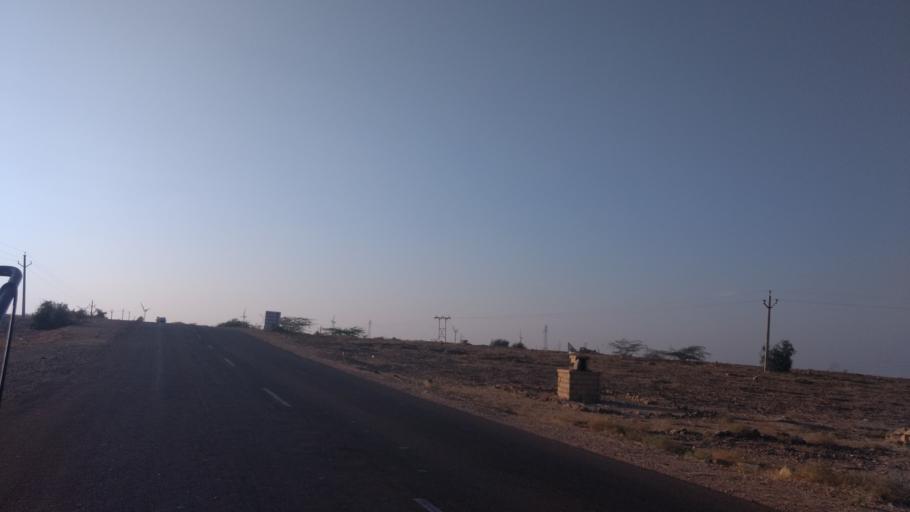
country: IN
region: Rajasthan
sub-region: Jaisalmer
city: Jaisalmer
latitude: 26.9197
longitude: 70.8225
